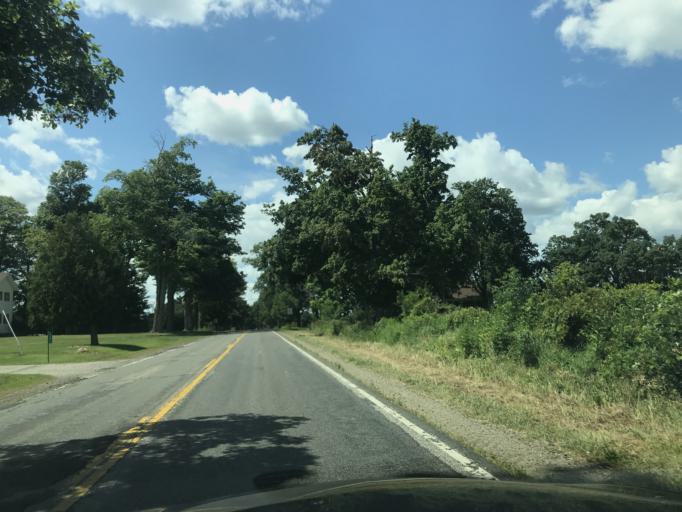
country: US
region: Michigan
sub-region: Ingham County
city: Leslie
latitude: 42.4512
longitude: -84.4741
